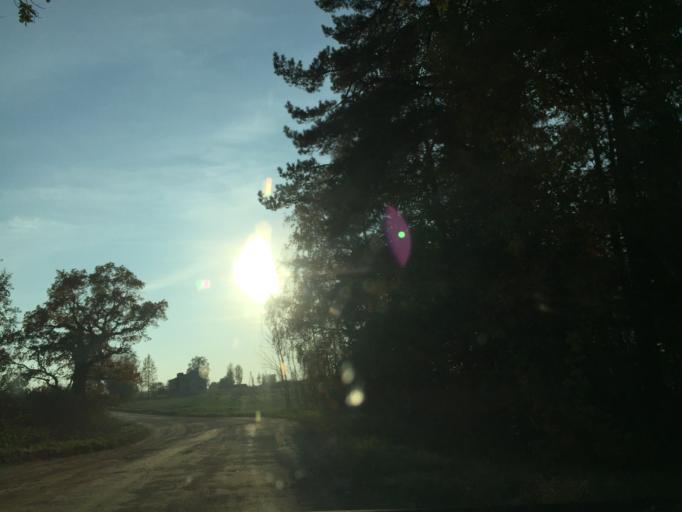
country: LV
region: Vainode
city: Vainode
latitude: 56.6195
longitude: 21.8174
